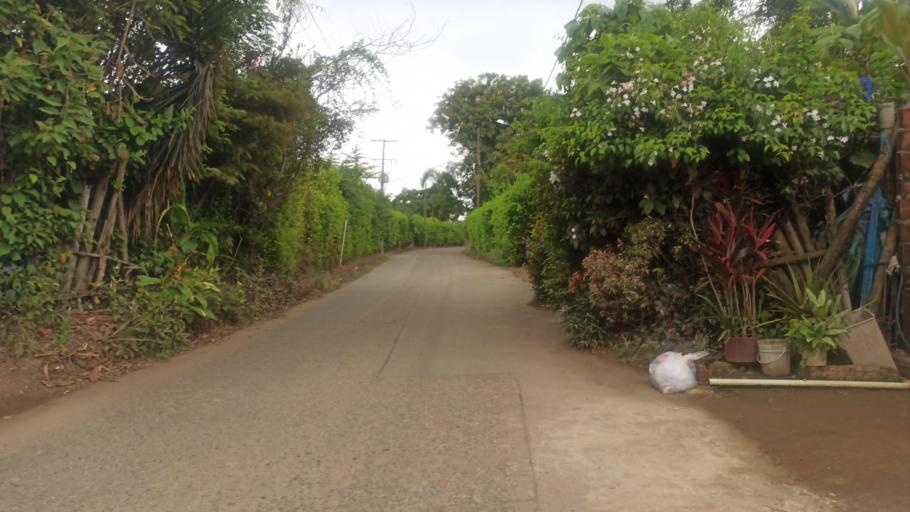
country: CO
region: Valle del Cauca
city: Jamundi
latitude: 3.2019
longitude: -76.5105
